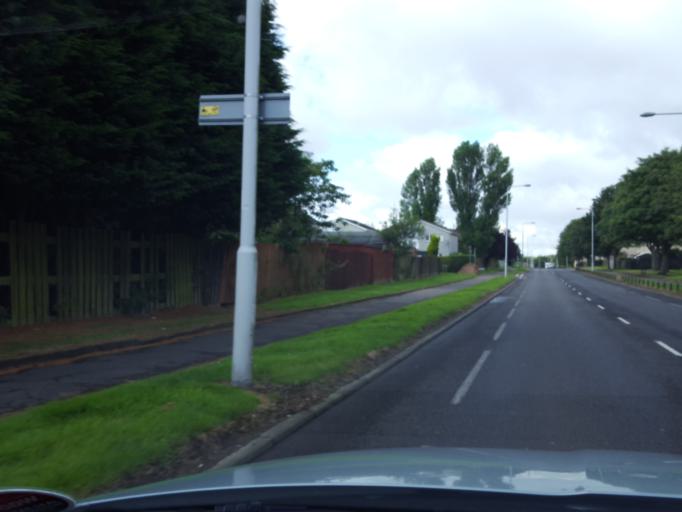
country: GB
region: Scotland
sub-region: Fife
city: Townhill
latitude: 56.0602
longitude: -3.4179
